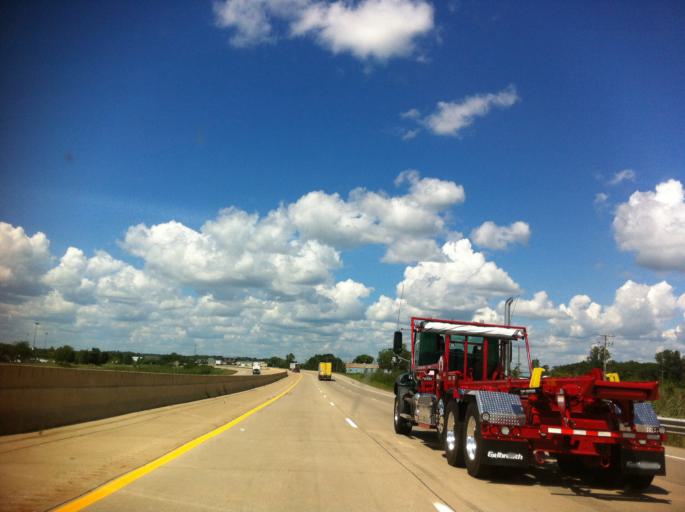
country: US
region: Michigan
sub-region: Monroe County
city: Dundee
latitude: 41.9619
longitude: -83.6725
